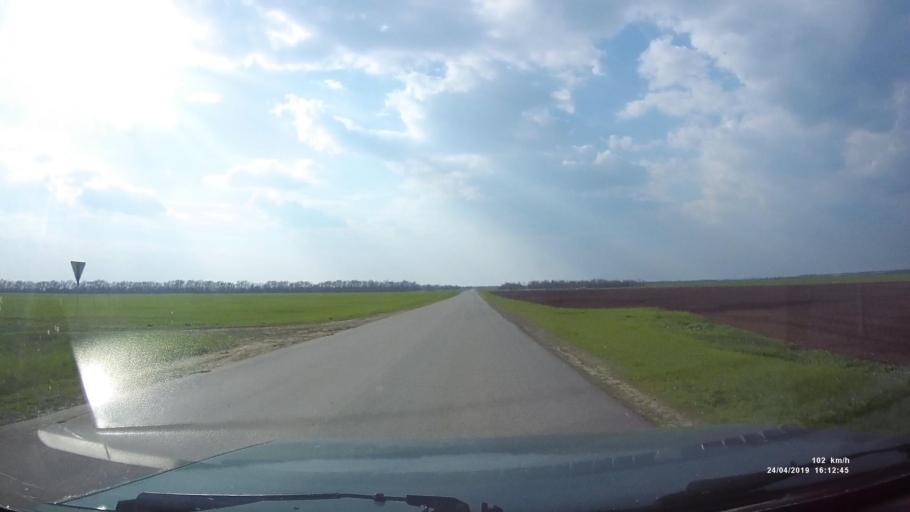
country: RU
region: Rostov
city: Sovetskoye
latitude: 46.7354
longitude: 42.2303
